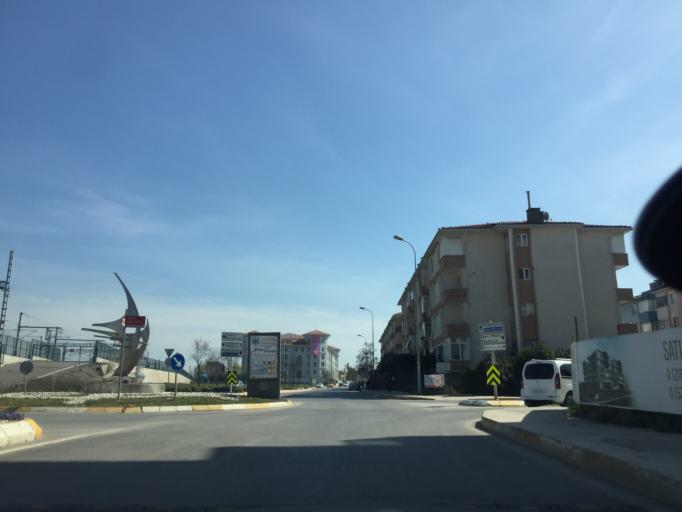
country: TR
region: Istanbul
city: Icmeler
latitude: 40.8341
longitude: 29.3155
